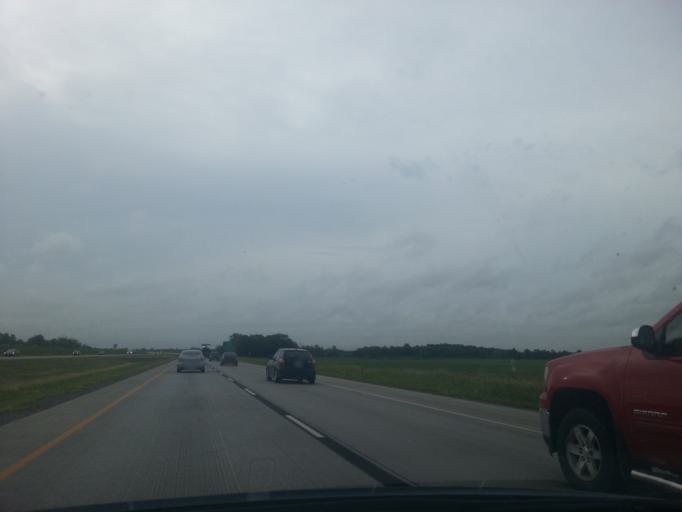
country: CA
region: Quebec
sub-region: Monteregie
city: Saint-Constant
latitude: 45.3590
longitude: -73.5757
